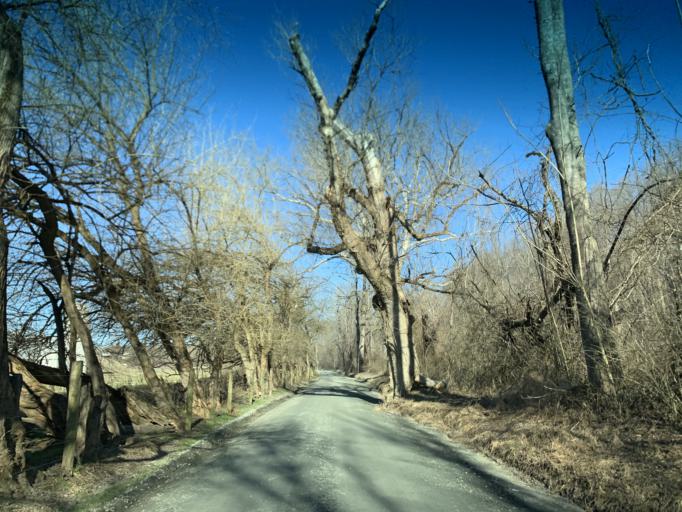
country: US
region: Maryland
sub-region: Harford County
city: Bel Air North
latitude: 39.6172
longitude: -76.3274
